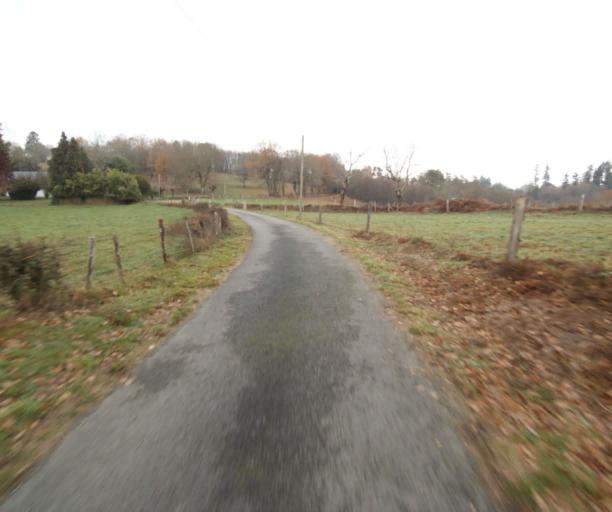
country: FR
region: Limousin
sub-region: Departement de la Correze
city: Chameyrat
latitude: 45.2278
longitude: 1.6980
